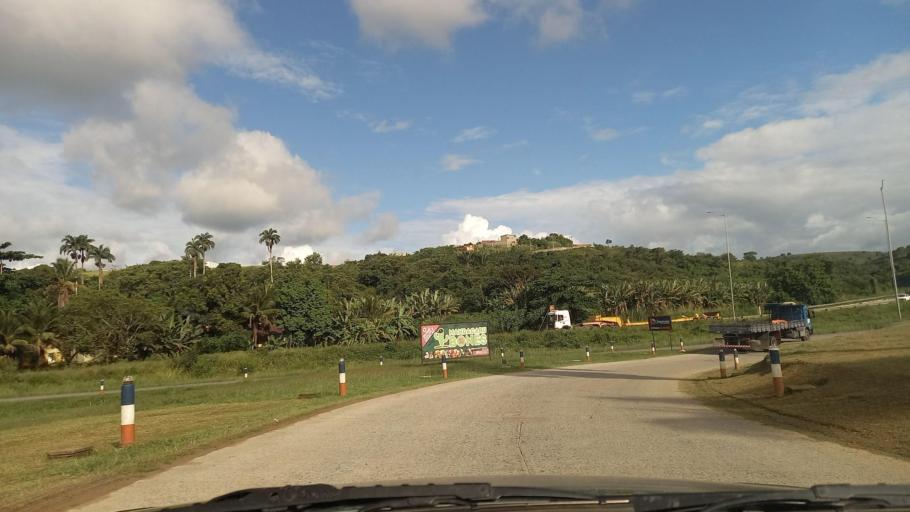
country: BR
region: Pernambuco
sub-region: Palmares
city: Palmares
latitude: -8.6909
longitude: -35.6085
